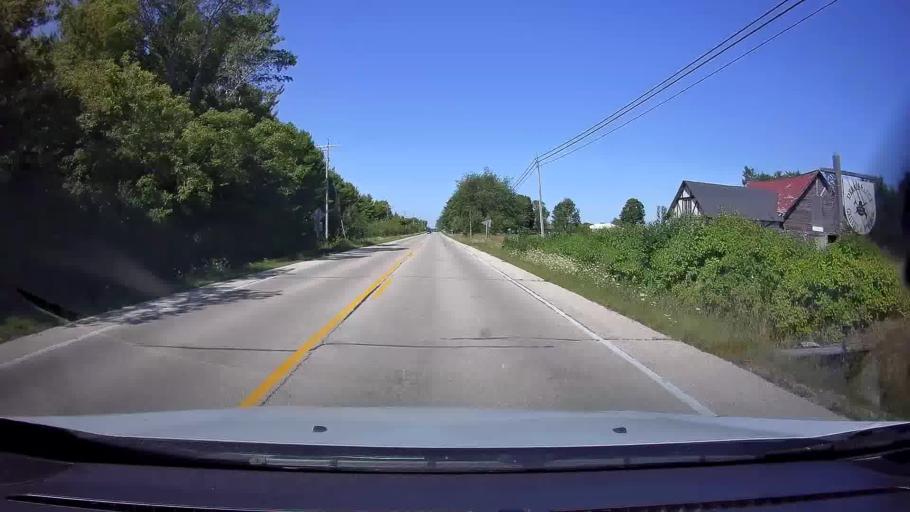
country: US
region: Michigan
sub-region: Delta County
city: Escanaba
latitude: 45.2647
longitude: -87.0194
